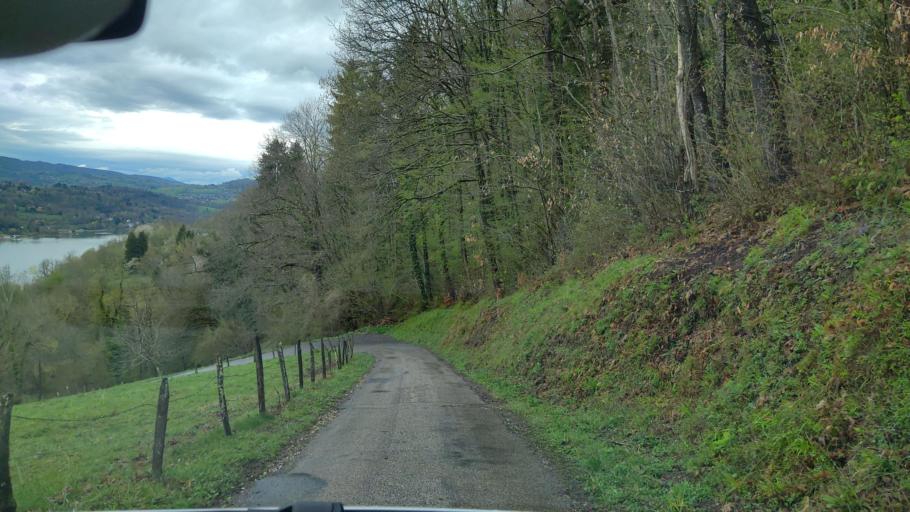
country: FR
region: Rhone-Alpes
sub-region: Departement de la Savoie
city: Vimines
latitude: 45.5518
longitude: 5.8131
